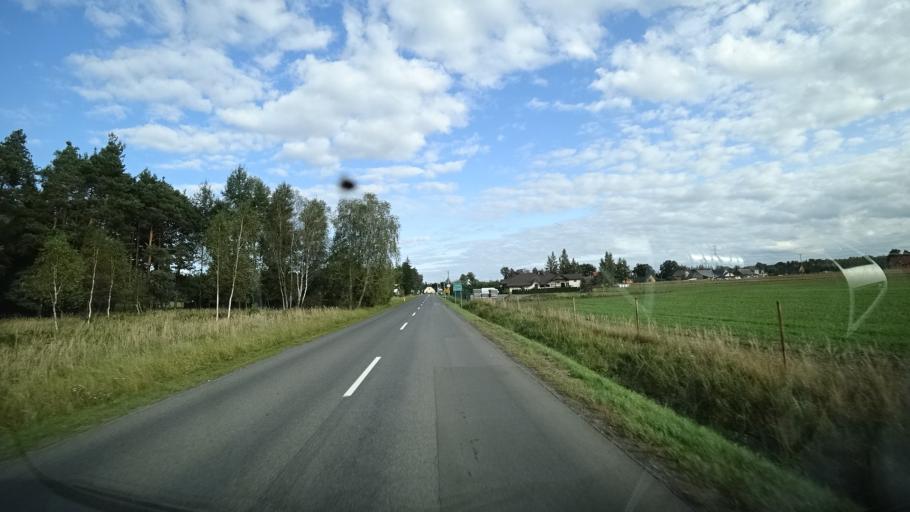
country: PL
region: Silesian Voivodeship
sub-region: Powiat gliwicki
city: Rudziniec
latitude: 50.2697
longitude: 18.4089
